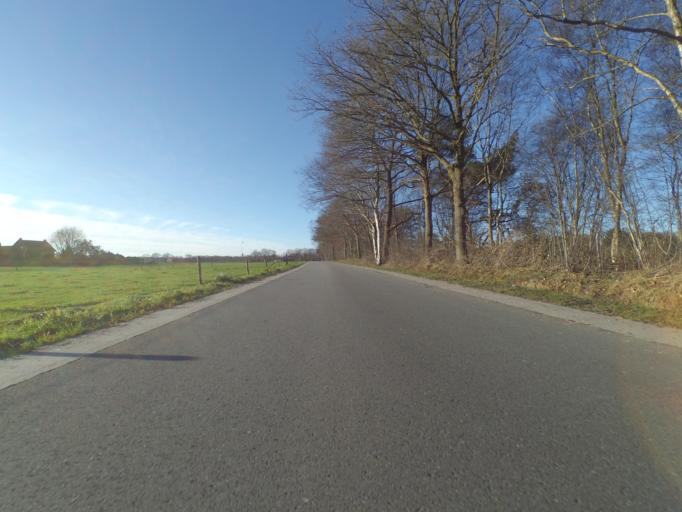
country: NL
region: Gelderland
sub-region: Gemeente Putten
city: Putten
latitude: 52.2429
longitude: 5.5603
